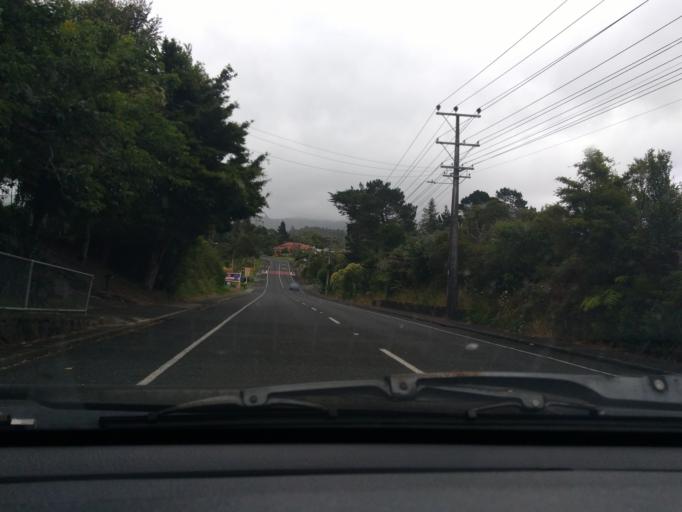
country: NZ
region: Auckland
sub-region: Auckland
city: Waitakere
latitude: -36.9129
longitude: 174.6193
